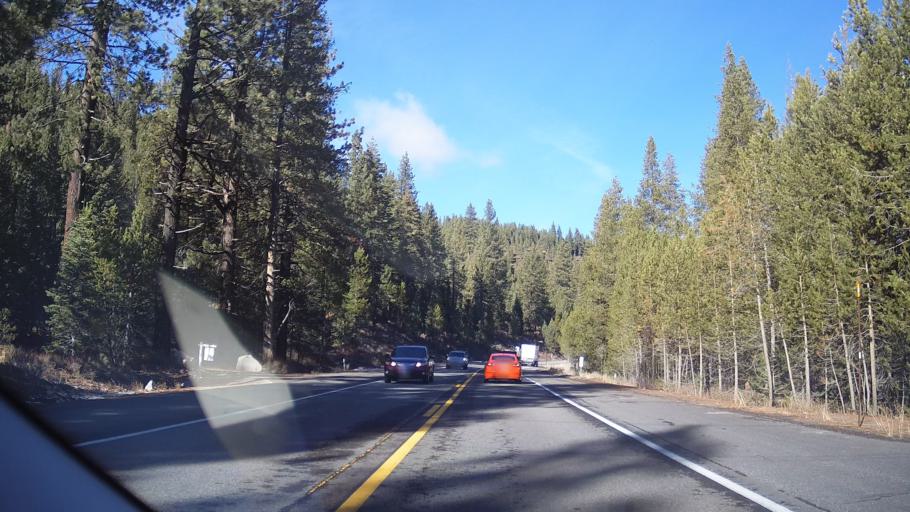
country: US
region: California
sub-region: Nevada County
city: Truckee
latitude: 39.2857
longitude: -120.2082
